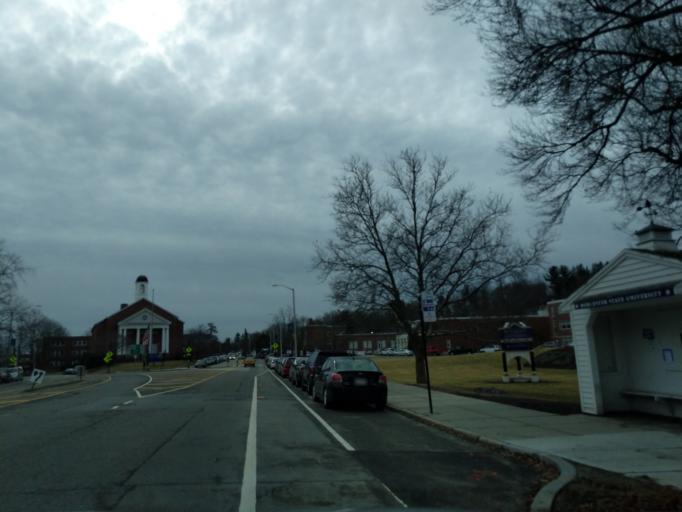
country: US
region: Massachusetts
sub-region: Worcester County
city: Worcester
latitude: 42.2685
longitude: -71.8411
